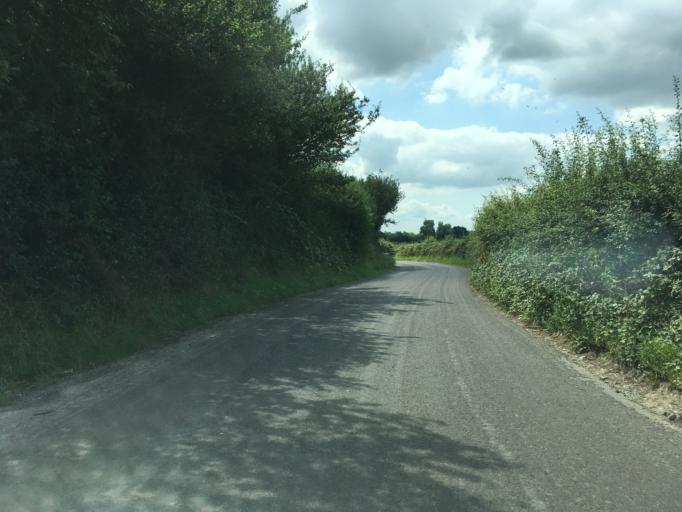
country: GB
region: England
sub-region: Gloucestershire
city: Gloucester
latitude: 51.8978
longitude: -2.2524
